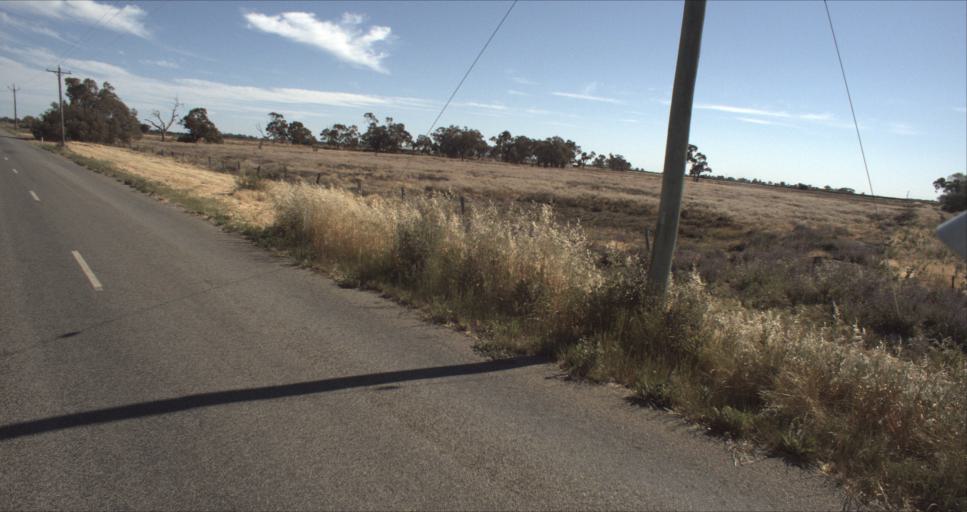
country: AU
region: New South Wales
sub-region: Leeton
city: Leeton
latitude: -34.5679
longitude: 146.3822
